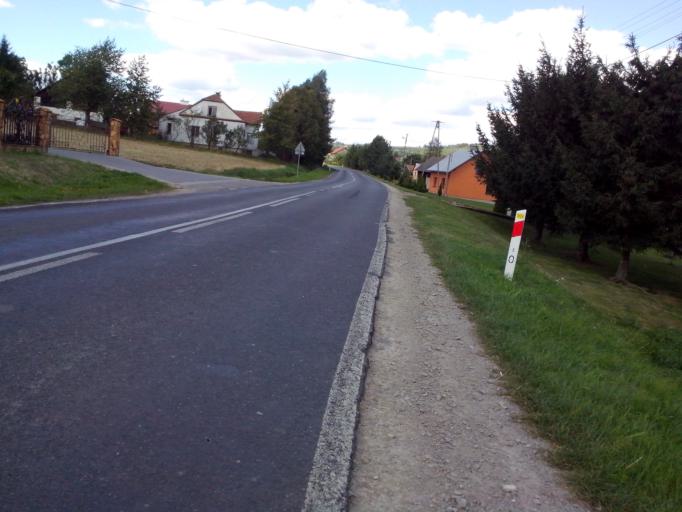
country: PL
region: Subcarpathian Voivodeship
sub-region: Powiat strzyzowski
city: Strzyzow
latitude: 49.8360
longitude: 21.8247
